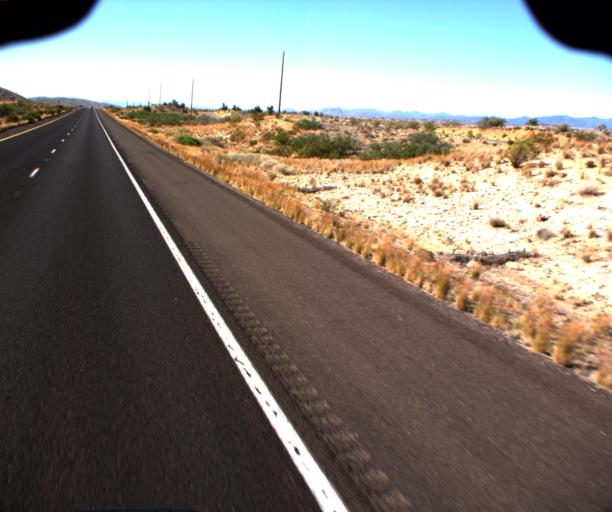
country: US
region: Arizona
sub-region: Mohave County
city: Kingman
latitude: 35.0329
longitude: -113.6650
